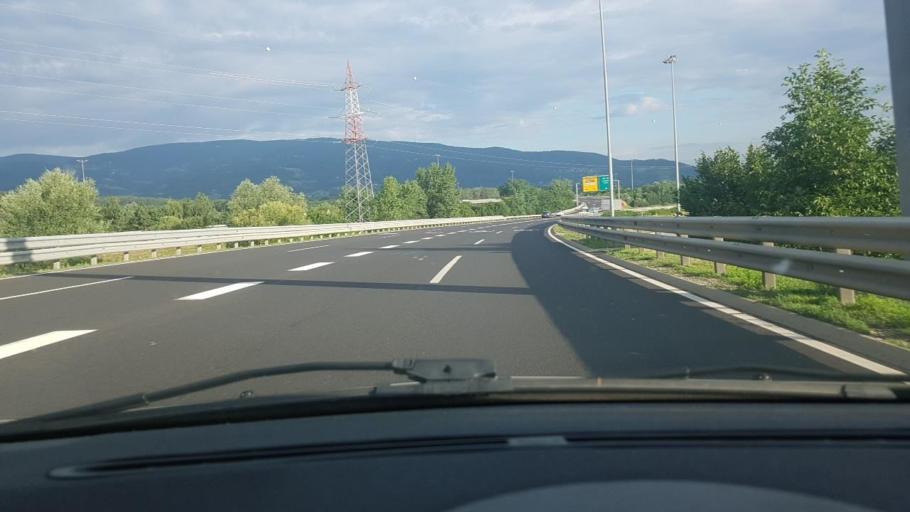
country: SI
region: Hoce-Slivnica
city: Radizel
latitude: 46.4806
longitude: 15.6623
